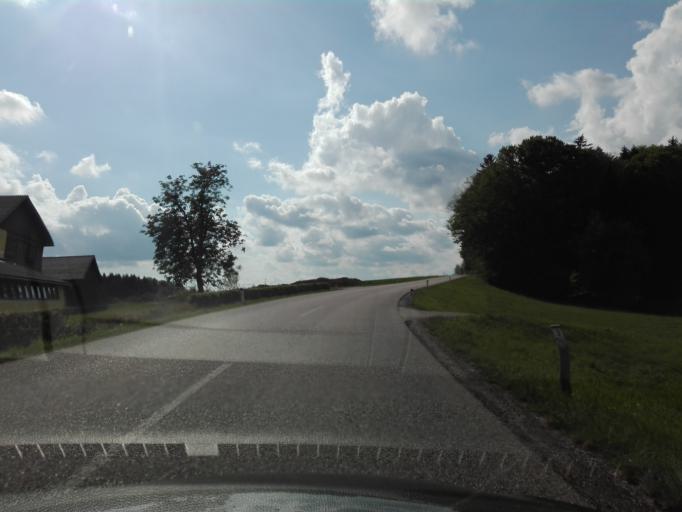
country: AT
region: Upper Austria
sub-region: Politischer Bezirk Rohrbach
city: Pfarrkirchen im Muehlkreis
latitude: 48.4377
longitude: 13.8121
